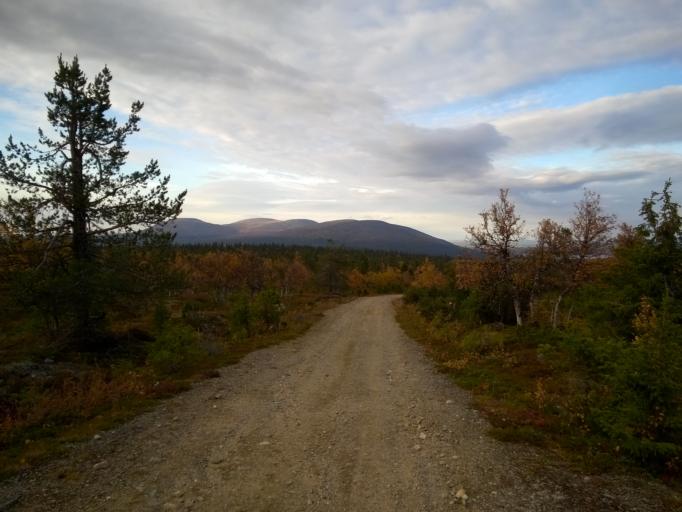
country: FI
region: Lapland
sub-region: Tunturi-Lappi
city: Muonio
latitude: 67.9896
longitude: 24.1119
